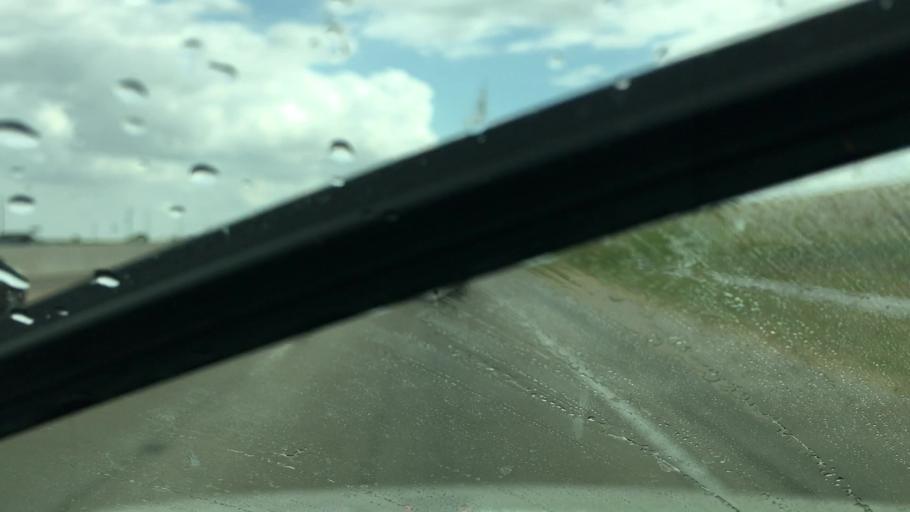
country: US
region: Texas
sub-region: McLennan County
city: Lorena
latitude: 31.3599
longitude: -97.2181
